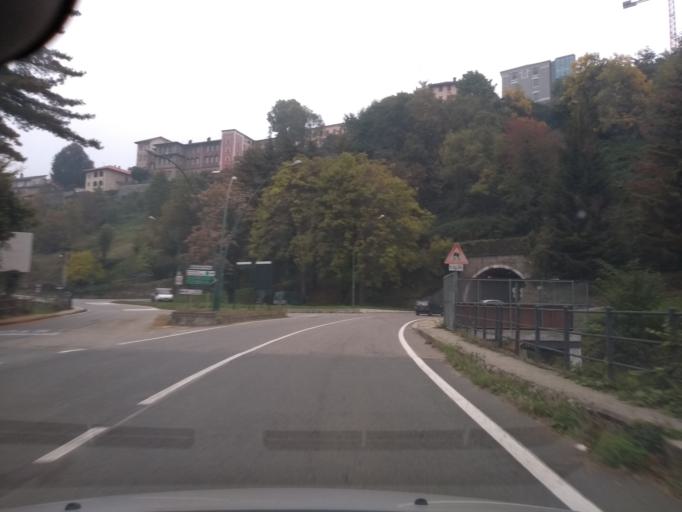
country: IT
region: Piedmont
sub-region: Provincia di Torino
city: Lanzo Torinese
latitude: 45.2698
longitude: 7.4773
